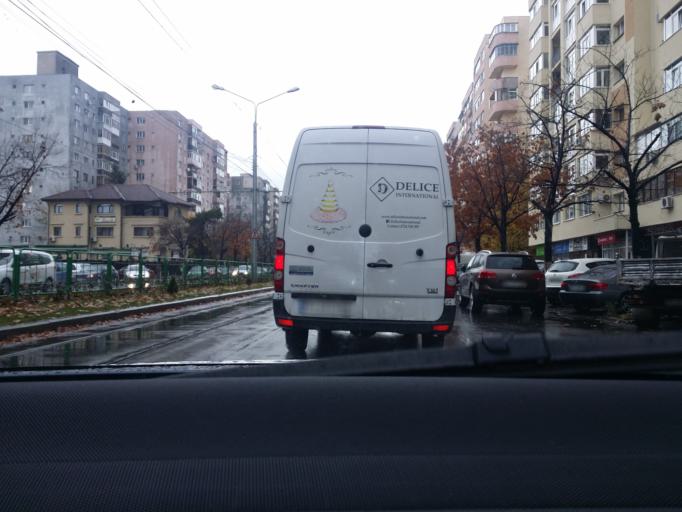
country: RO
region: Prahova
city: Ploiesti
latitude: 44.9493
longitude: 26.0058
